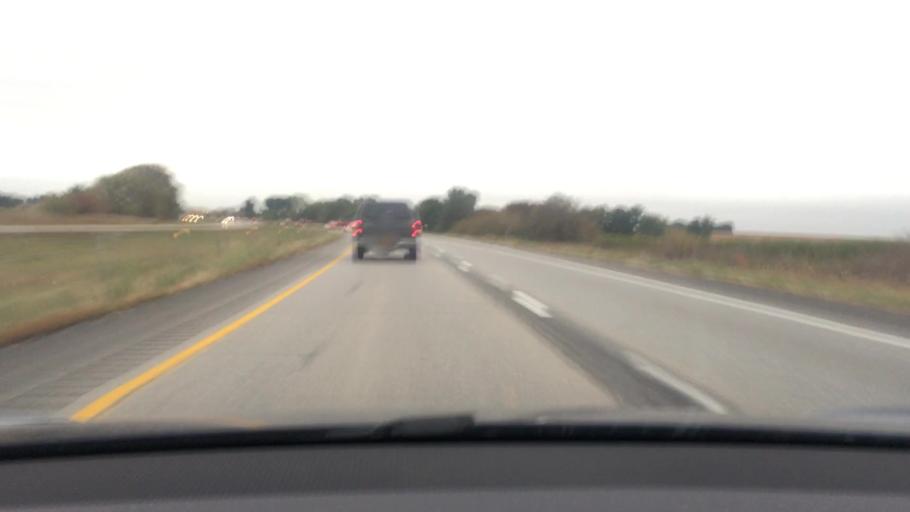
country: US
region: Iowa
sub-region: Johnson County
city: North Liberty
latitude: 41.7743
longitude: -91.6468
